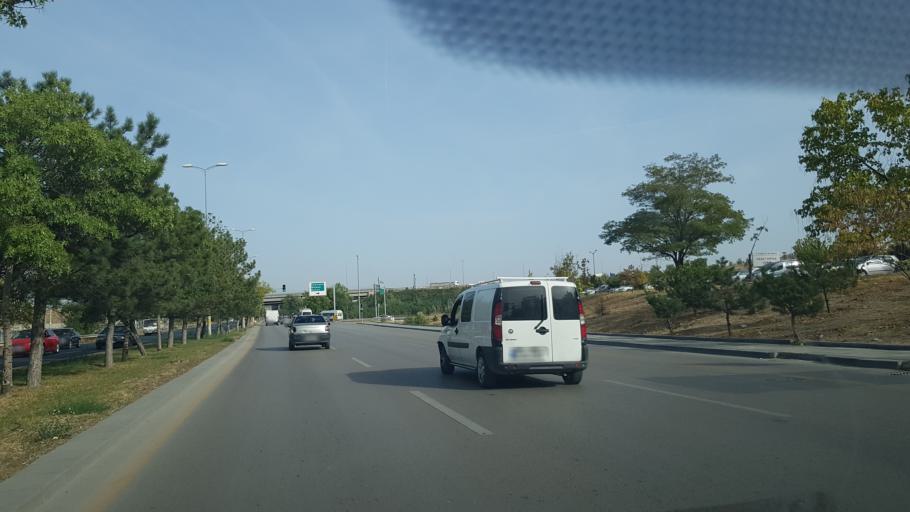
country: TR
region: Ankara
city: Etimesgut
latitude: 39.9565
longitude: 32.6192
